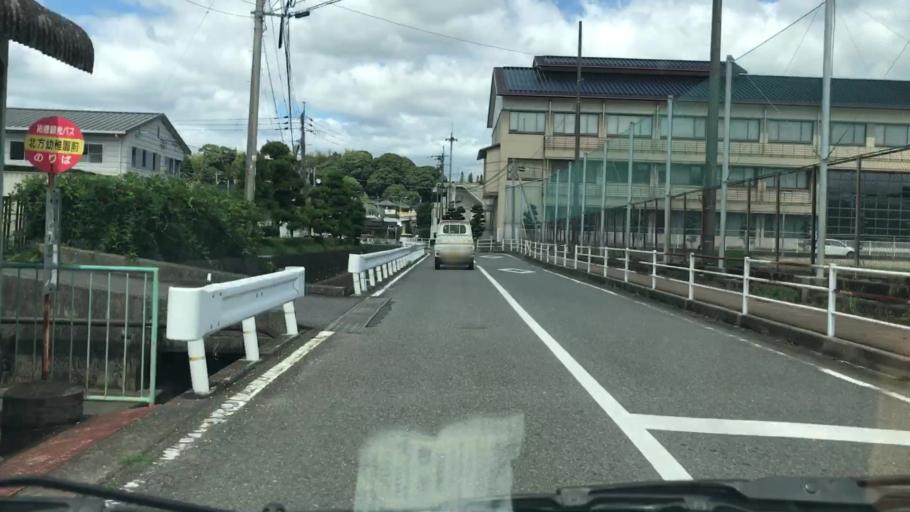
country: JP
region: Saga Prefecture
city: Takeocho-takeo
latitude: 33.2188
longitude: 130.0684
